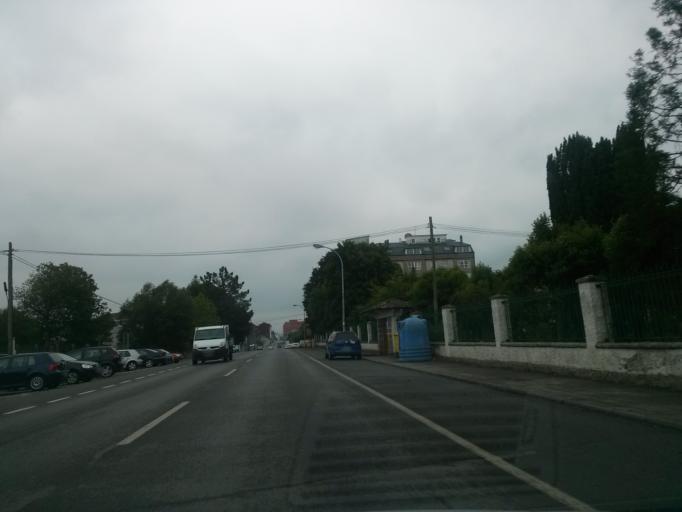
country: ES
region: Galicia
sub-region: Provincia de Lugo
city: Rabade
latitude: 43.1233
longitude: -7.6337
